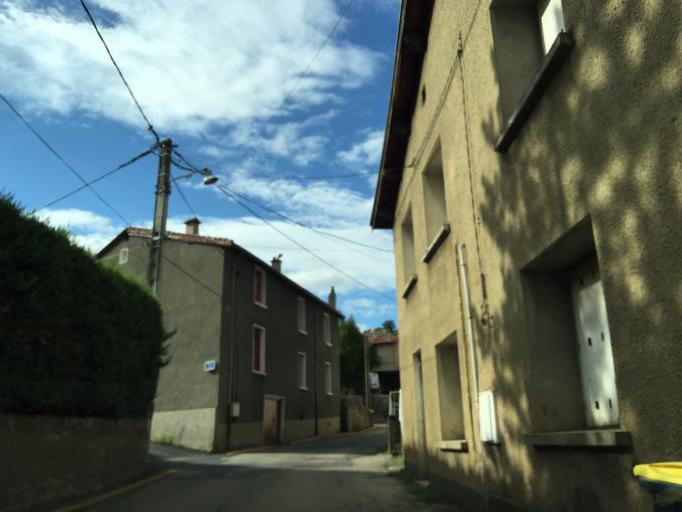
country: FR
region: Rhone-Alpes
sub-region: Departement de la Loire
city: La Grand-Croix
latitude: 45.4966
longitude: 4.5555
